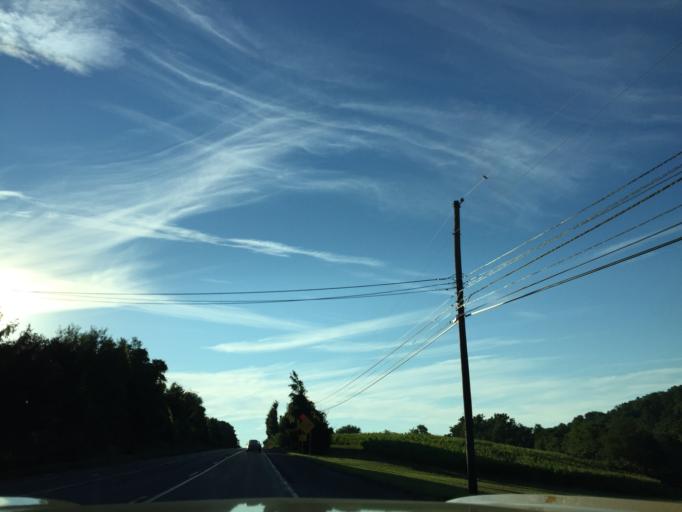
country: US
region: Pennsylvania
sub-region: Lehigh County
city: Breinigsville
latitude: 40.5431
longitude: -75.6602
